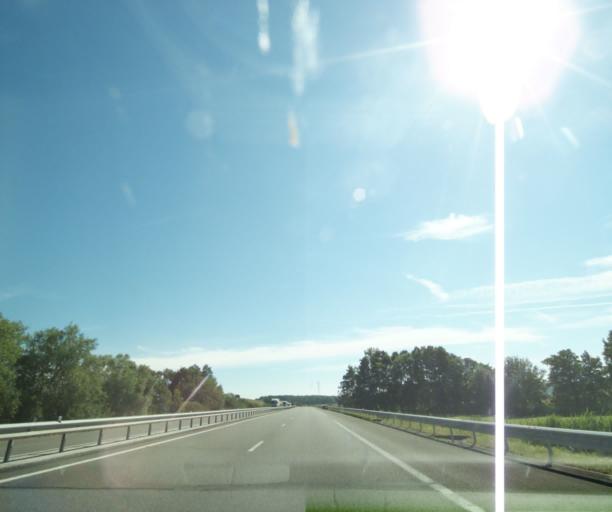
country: FR
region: Lorraine
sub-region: Departement des Vosges
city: Bulgneville
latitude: 48.1920
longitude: 5.7728
